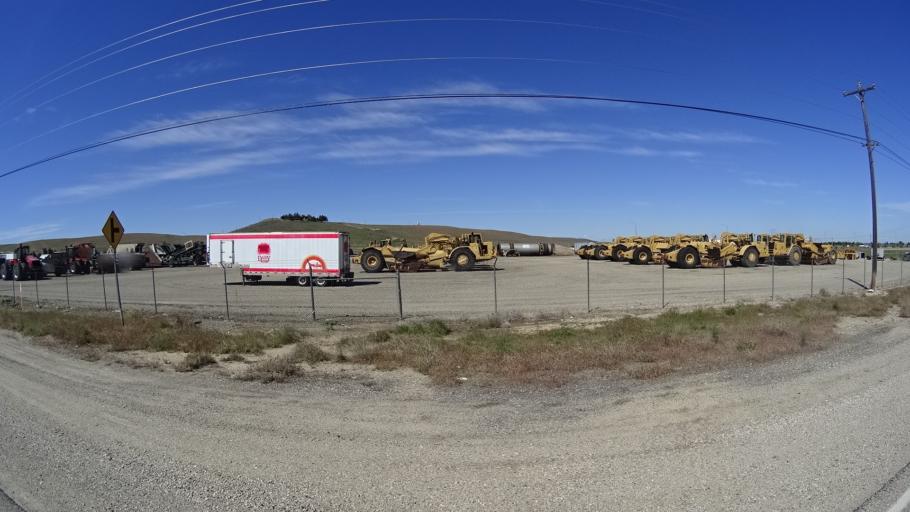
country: US
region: Idaho
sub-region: Ada County
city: Boise
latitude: 43.5138
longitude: -116.1436
